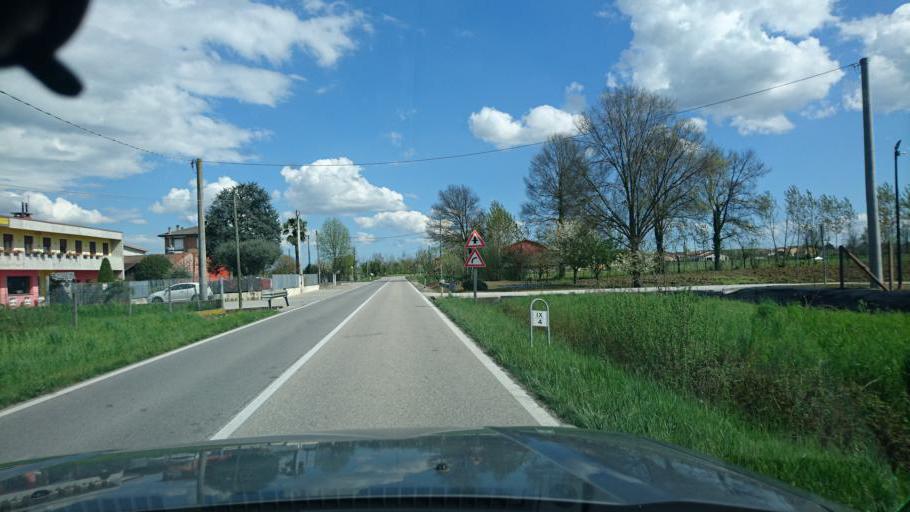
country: IT
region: Veneto
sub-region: Provincia di Padova
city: Cavino
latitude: 45.5131
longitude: 11.8896
